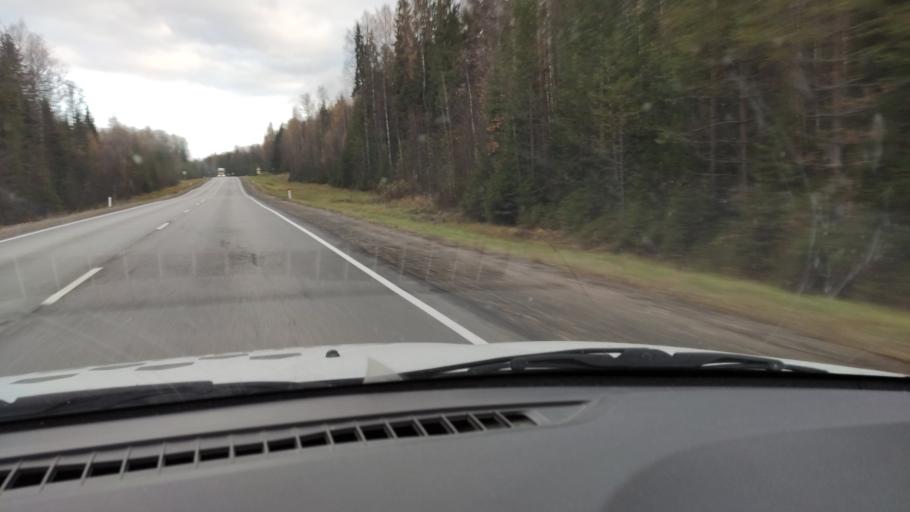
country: RU
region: Kirov
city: Chernaya Kholunitsa
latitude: 58.8353
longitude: 51.7558
